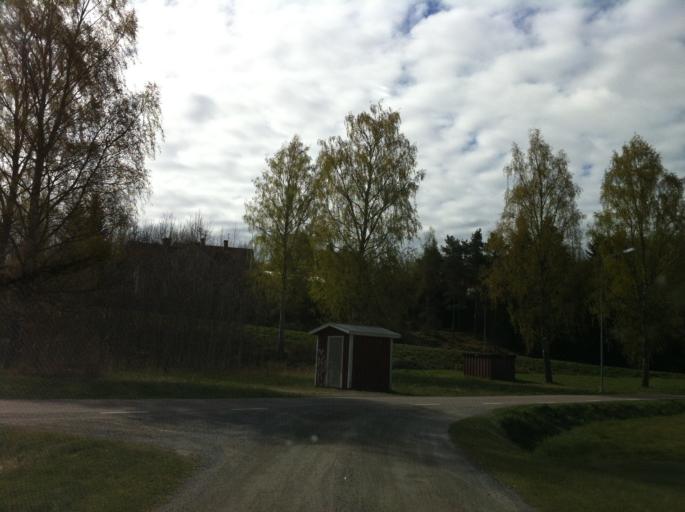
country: SE
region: OEstergoetland
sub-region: Valdemarsviks Kommun
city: Valdemarsvik
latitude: 58.1880
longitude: 16.7996
